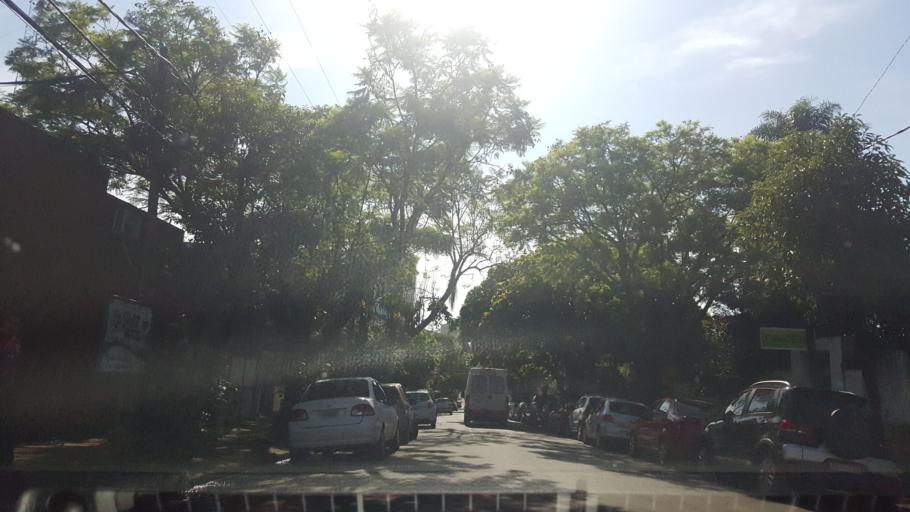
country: AR
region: Misiones
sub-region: Departamento de Capital
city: Posadas
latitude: -27.3737
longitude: -55.8934
